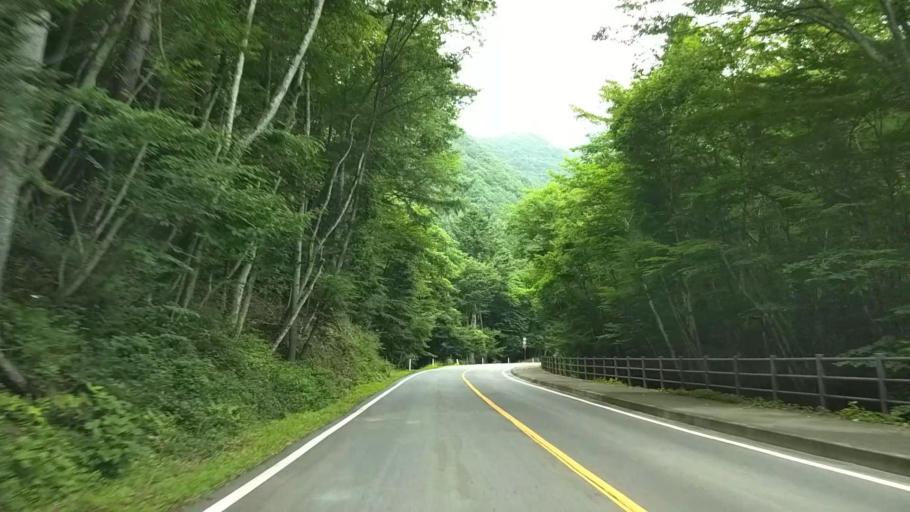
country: JP
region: Yamanashi
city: Fujikawaguchiko
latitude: 35.4939
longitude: 138.6495
